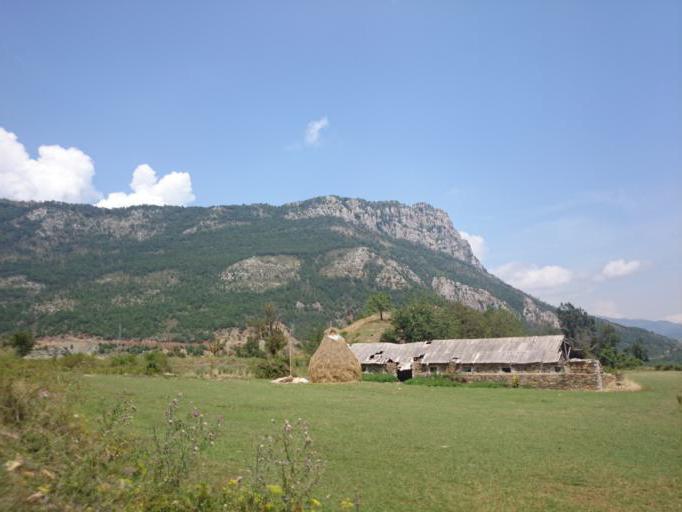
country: AL
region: Diber
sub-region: Rrethi i Dibres
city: Fushe-Lure
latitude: 41.8320
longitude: 20.1870
